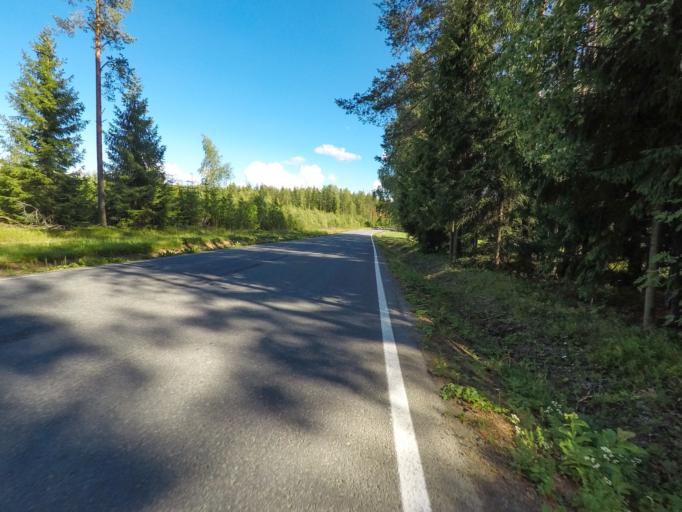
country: FI
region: South Karelia
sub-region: Lappeenranta
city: Taipalsaari
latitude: 61.1792
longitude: 28.0067
